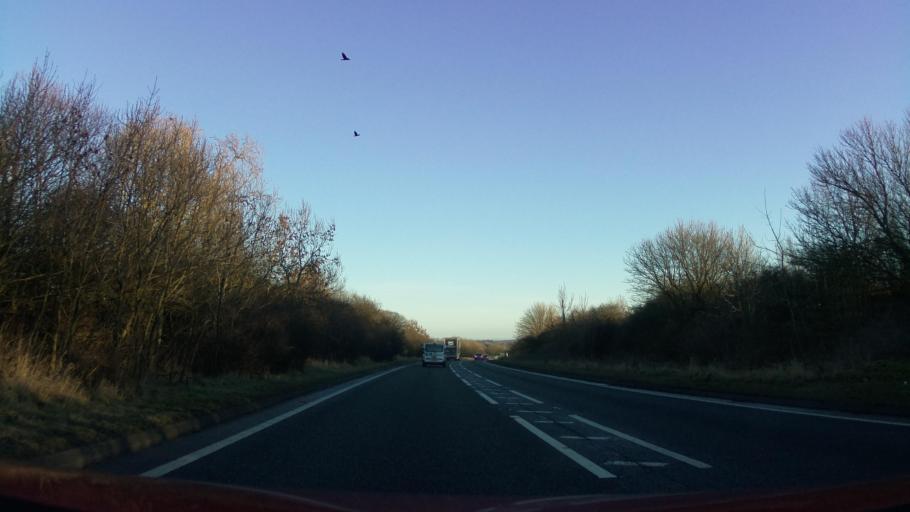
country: GB
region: England
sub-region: County Durham
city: Bowes
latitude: 54.5193
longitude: -2.0025
